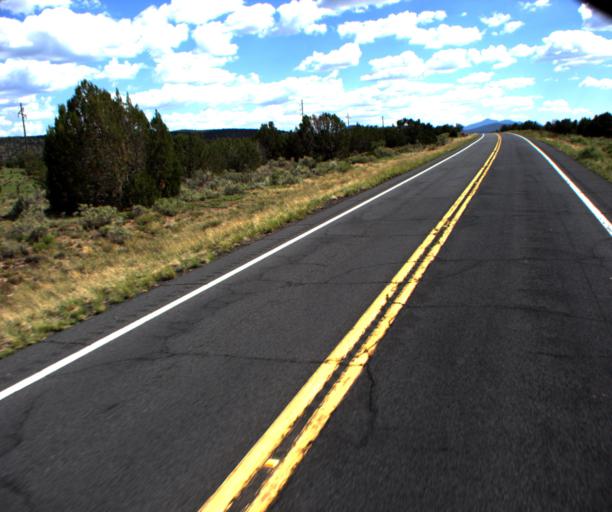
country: US
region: Arizona
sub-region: Coconino County
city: Williams
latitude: 35.5078
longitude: -112.1734
